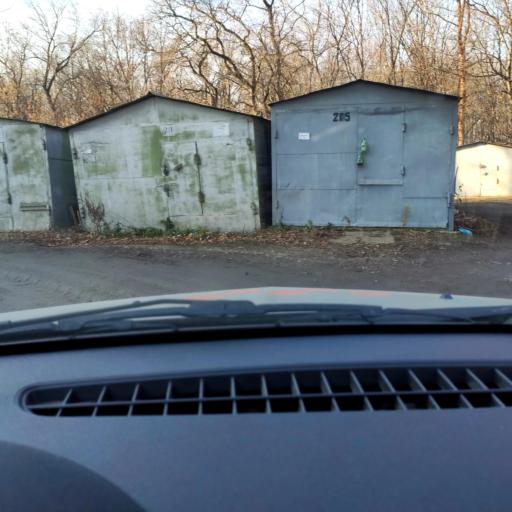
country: RU
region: Bashkortostan
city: Ufa
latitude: 54.7911
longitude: 56.0268
